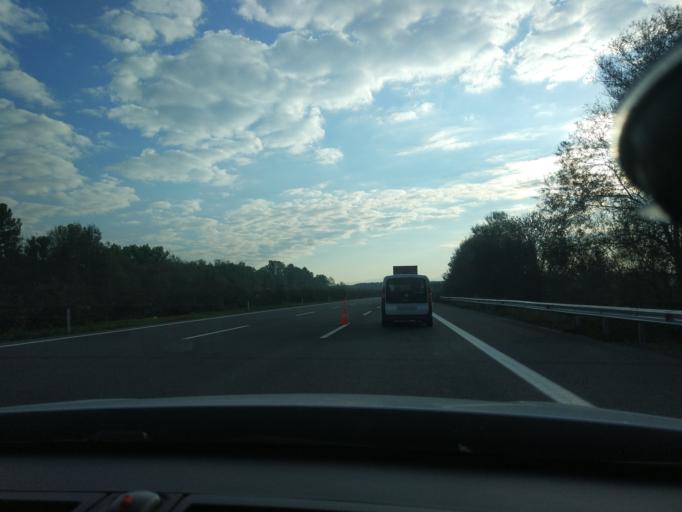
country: TR
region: Duzce
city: Duzce
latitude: 40.8108
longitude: 31.1312
